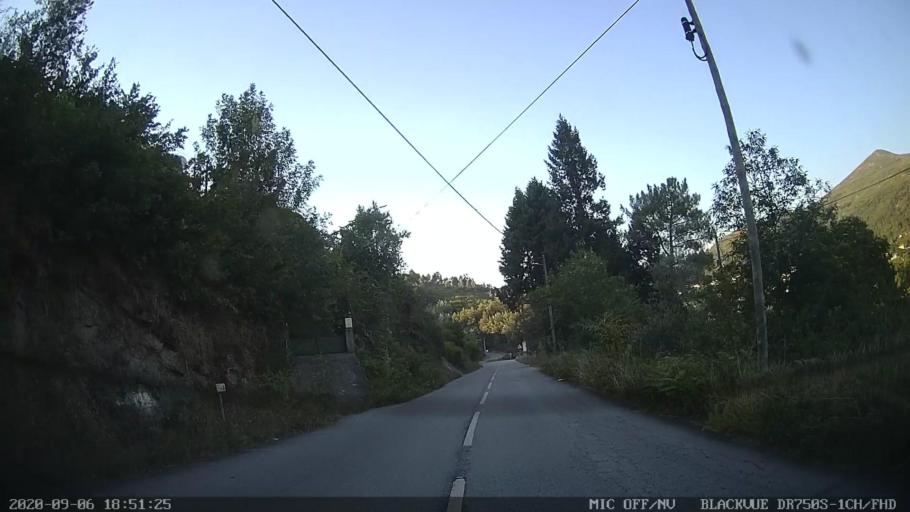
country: PT
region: Porto
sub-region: Amarante
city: Amarante
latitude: 41.2579
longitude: -7.9918
